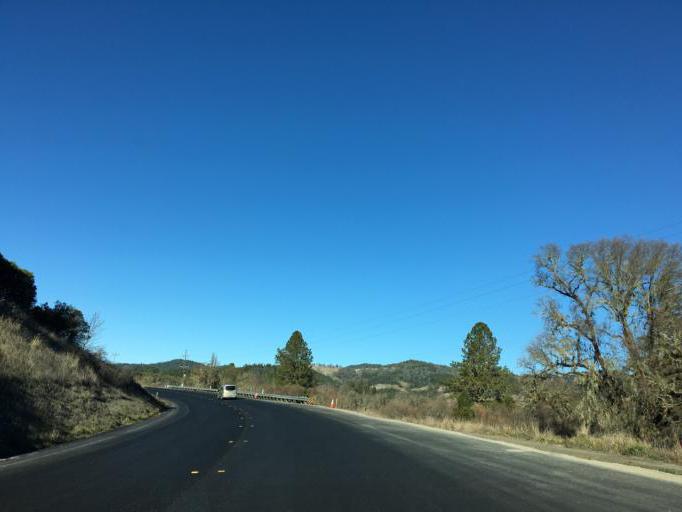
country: US
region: California
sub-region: Mendocino County
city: Laytonville
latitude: 39.6275
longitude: -123.4624
